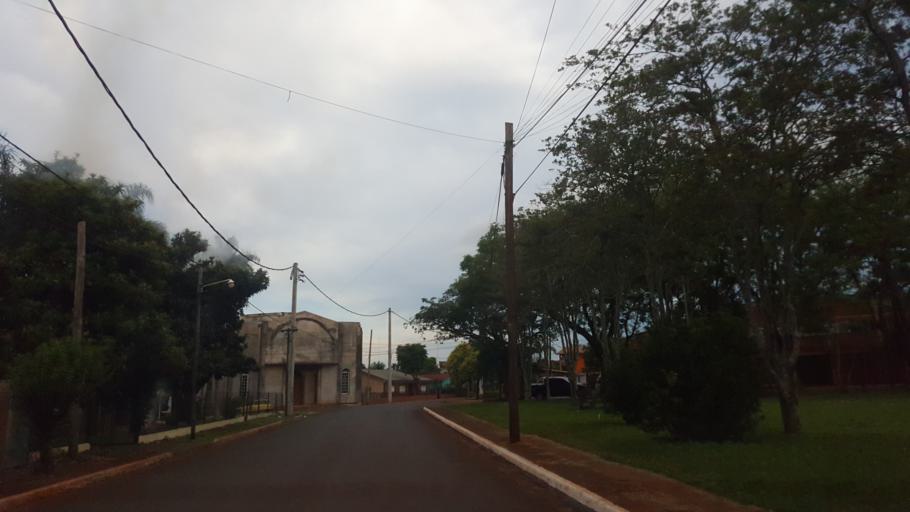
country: AR
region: Misiones
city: Jardin America
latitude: -27.0460
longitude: -55.2372
